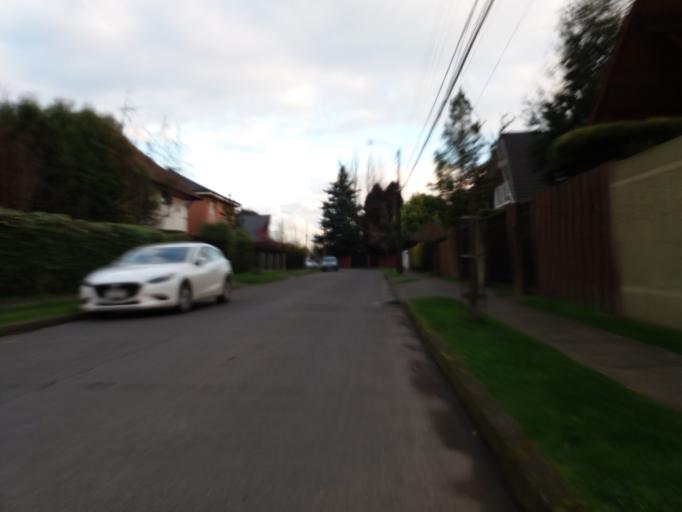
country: CL
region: Araucania
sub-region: Provincia de Cautin
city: Temuco
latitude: -38.7386
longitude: -72.6082
